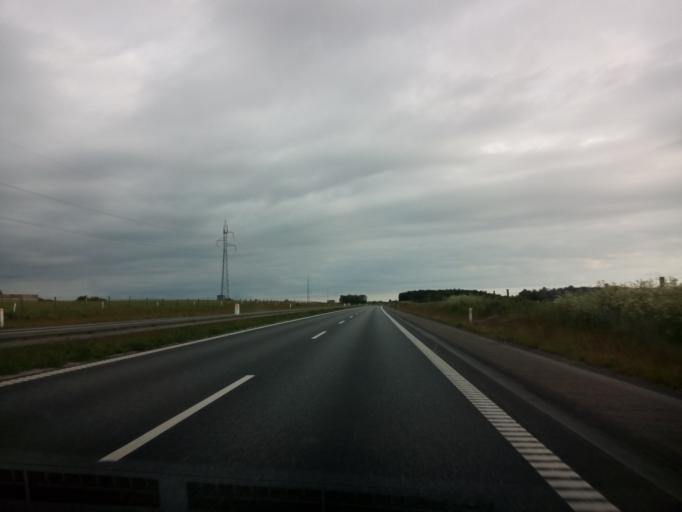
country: DK
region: North Denmark
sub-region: Hjorring Kommune
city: Vra
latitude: 57.3294
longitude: 10.0255
